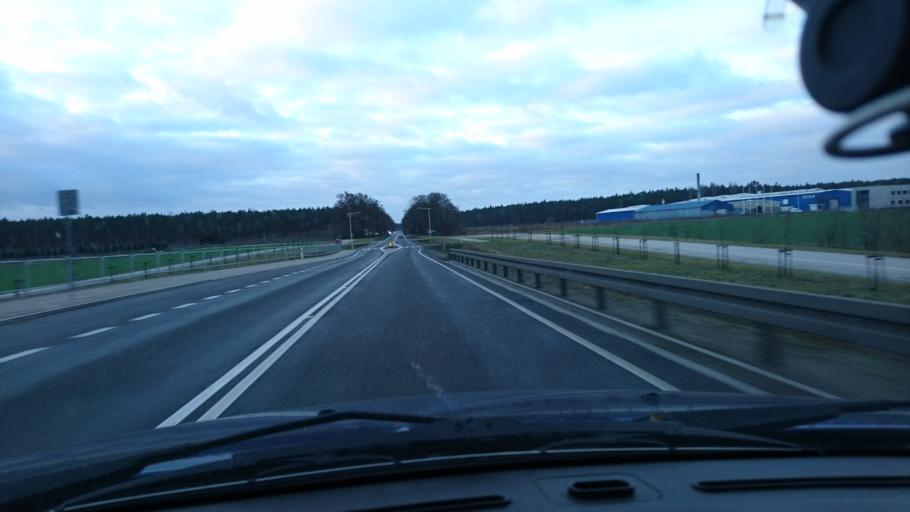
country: PL
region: Greater Poland Voivodeship
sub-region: Powiat kepinski
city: Kepno
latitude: 51.3188
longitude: 17.9765
